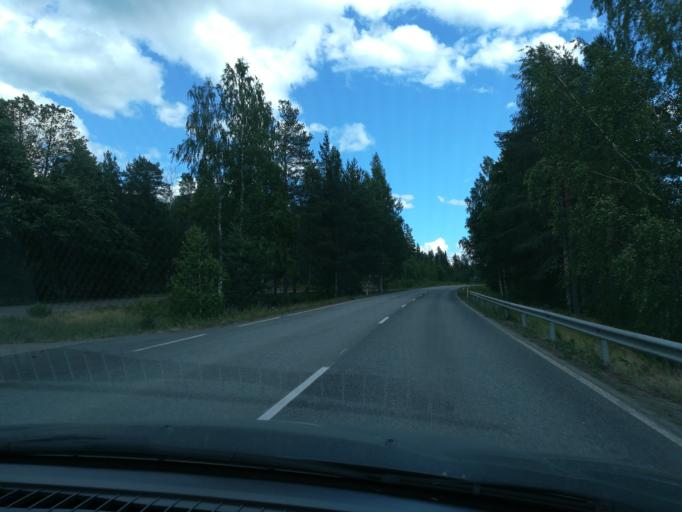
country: FI
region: Southern Savonia
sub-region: Mikkeli
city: Hirvensalmi
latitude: 61.6716
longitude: 26.8490
